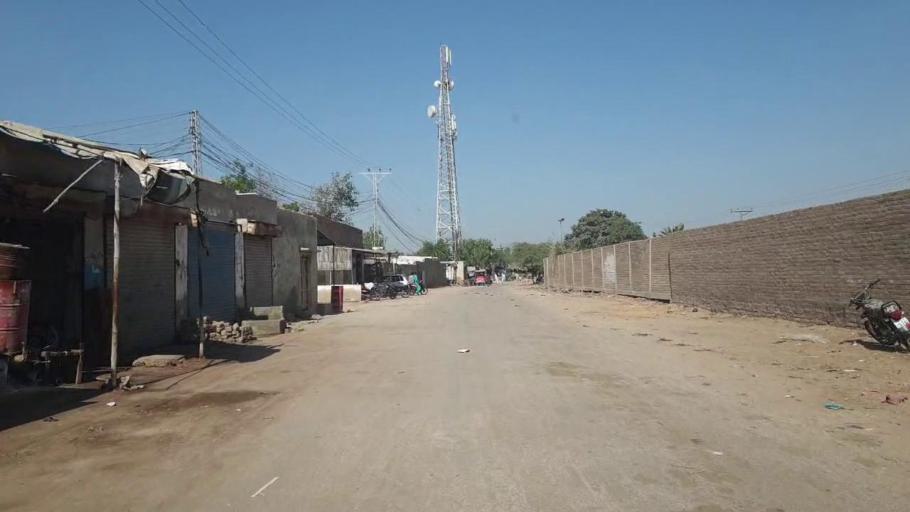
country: PK
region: Sindh
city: Talhar
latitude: 24.8823
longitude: 68.8193
